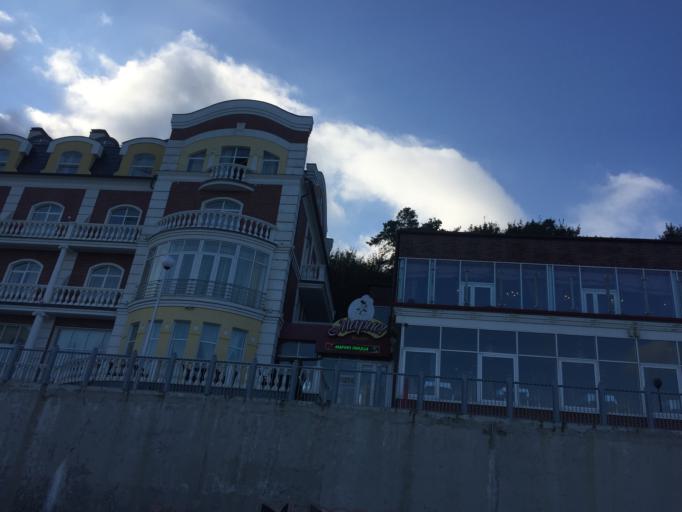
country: RU
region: Kaliningrad
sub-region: Gorod Svetlogorsk
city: Svetlogorsk
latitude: 54.9461
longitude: 20.1483
